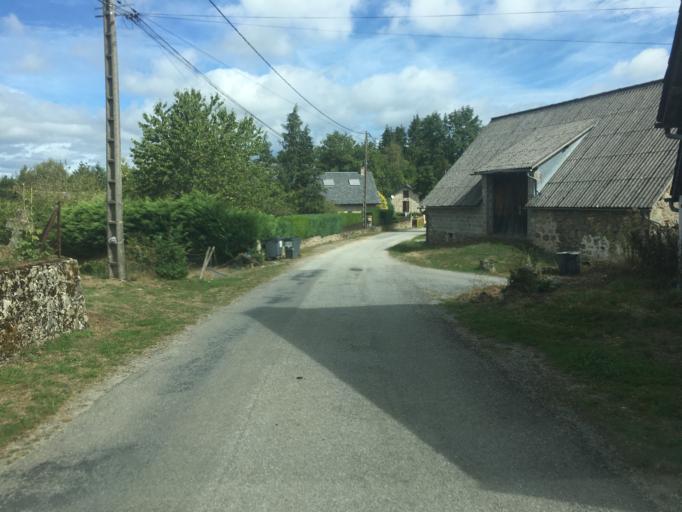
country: FR
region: Auvergne
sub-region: Departement du Cantal
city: Champagnac
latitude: 45.4144
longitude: 2.4001
